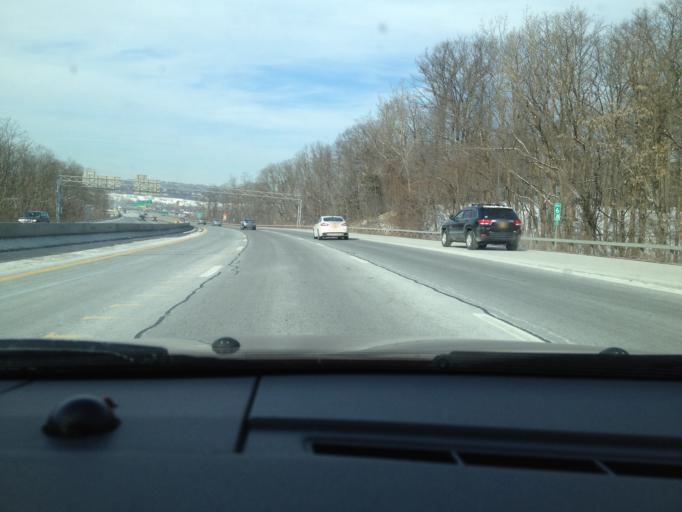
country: US
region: New York
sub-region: Rensselaer County
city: Rensselaer
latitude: 42.6615
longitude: -73.7230
